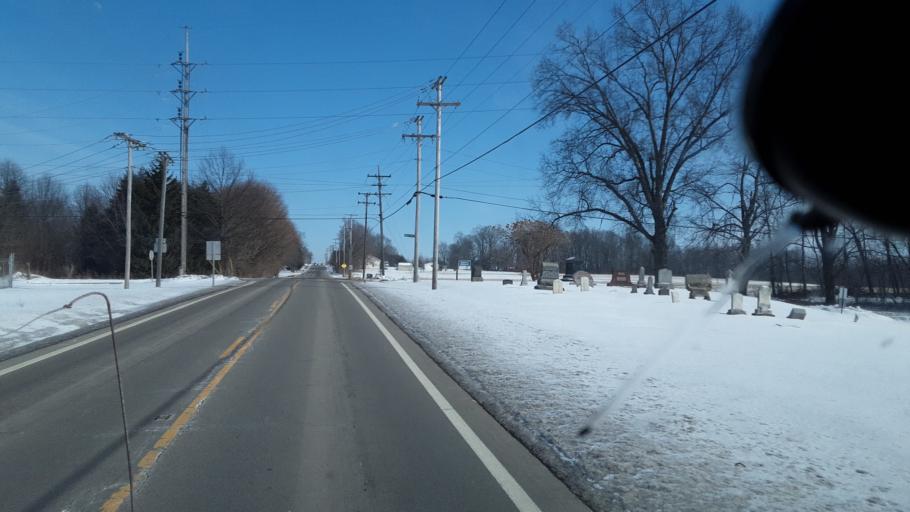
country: US
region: Ohio
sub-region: Columbiana County
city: Salem
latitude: 40.9440
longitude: -80.8030
